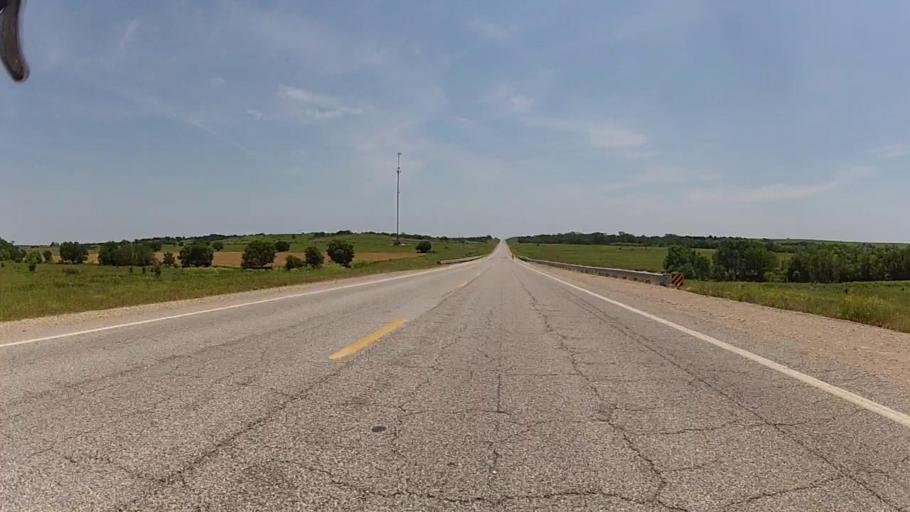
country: US
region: Kansas
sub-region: Chautauqua County
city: Sedan
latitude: 37.1132
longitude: -96.4596
